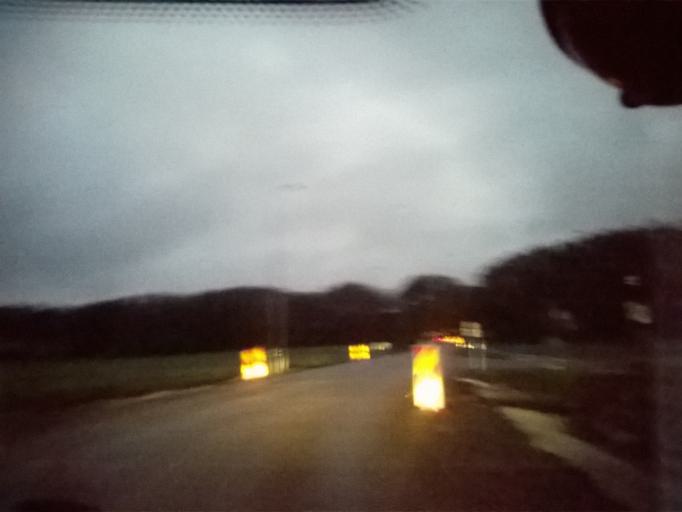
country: EE
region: Harju
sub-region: Viimsi vald
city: Viimsi
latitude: 59.5193
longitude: 24.8437
